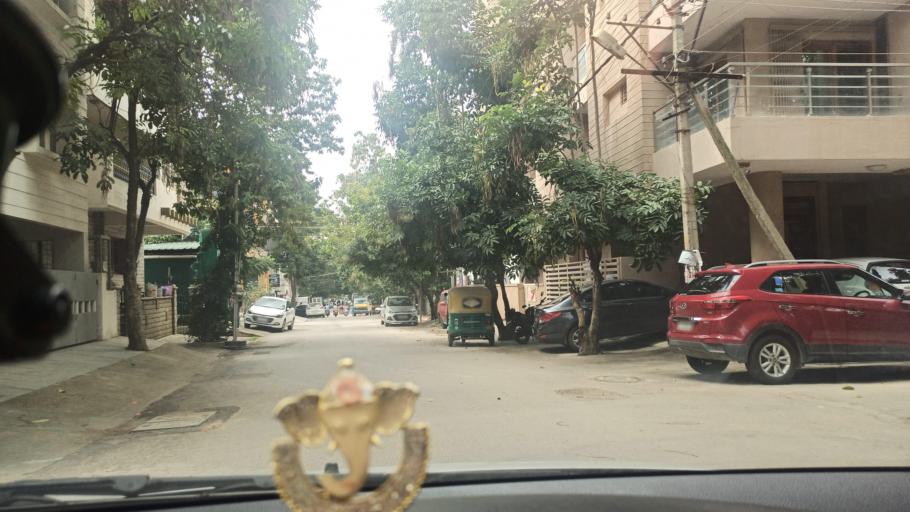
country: IN
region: Karnataka
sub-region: Bangalore Urban
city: Bangalore
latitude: 12.9173
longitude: 77.6504
